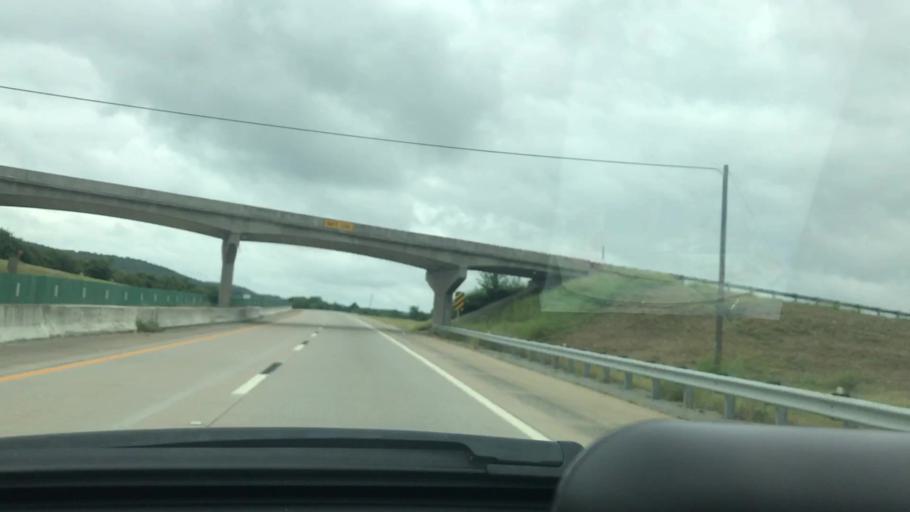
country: US
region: Oklahoma
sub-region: Pittsburg County
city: Krebs
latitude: 35.0575
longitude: -95.7068
